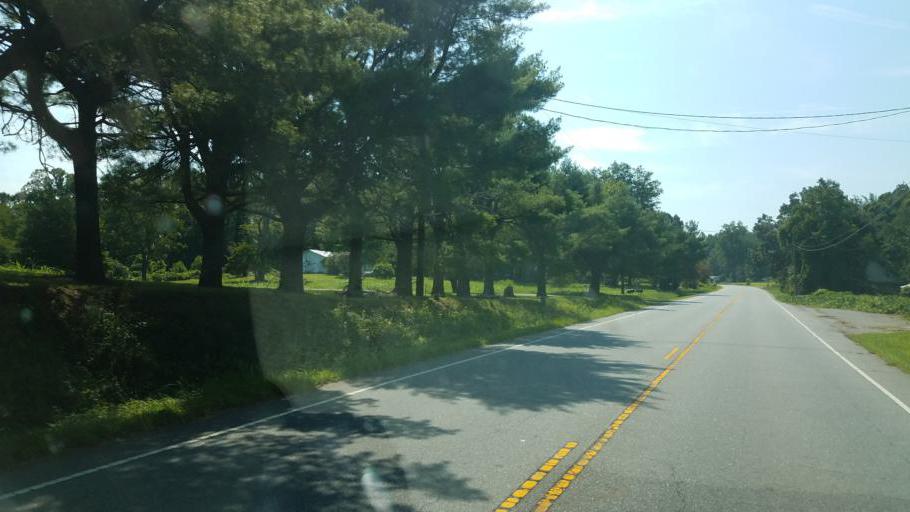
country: US
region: North Carolina
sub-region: Burke County
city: Glen Alpine
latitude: 35.7973
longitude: -81.7693
